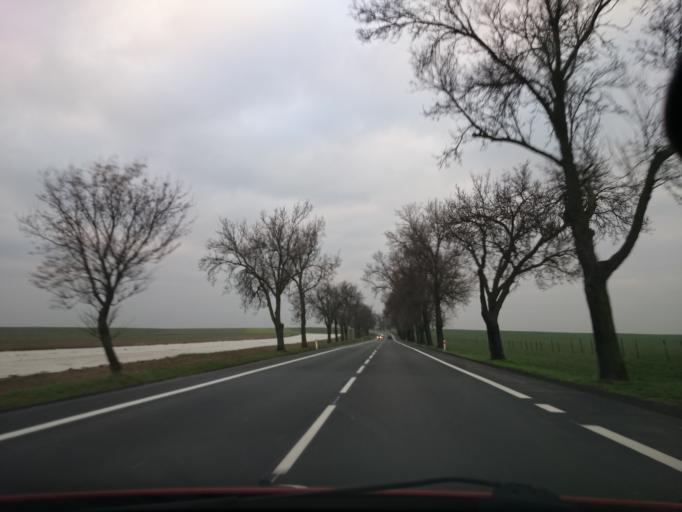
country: PL
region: Opole Voivodeship
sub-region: Powiat nyski
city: Sidzina
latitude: 50.5661
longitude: 17.4388
